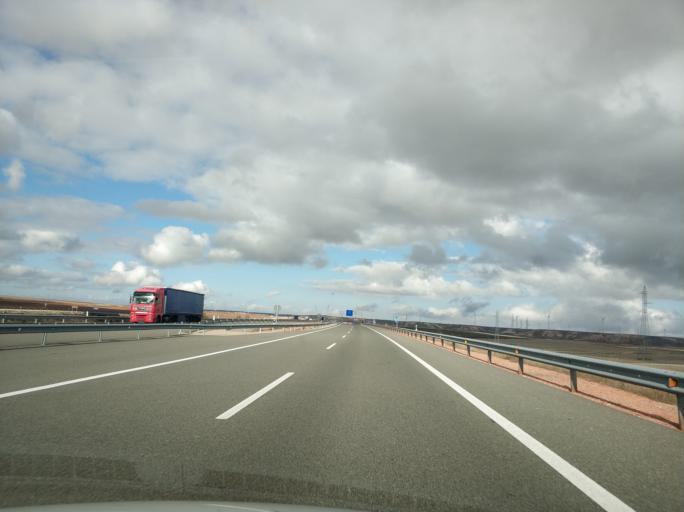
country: ES
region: Castille and Leon
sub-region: Provincia de Soria
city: Alcubilla de las Penas
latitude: 41.2519
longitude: -2.4738
